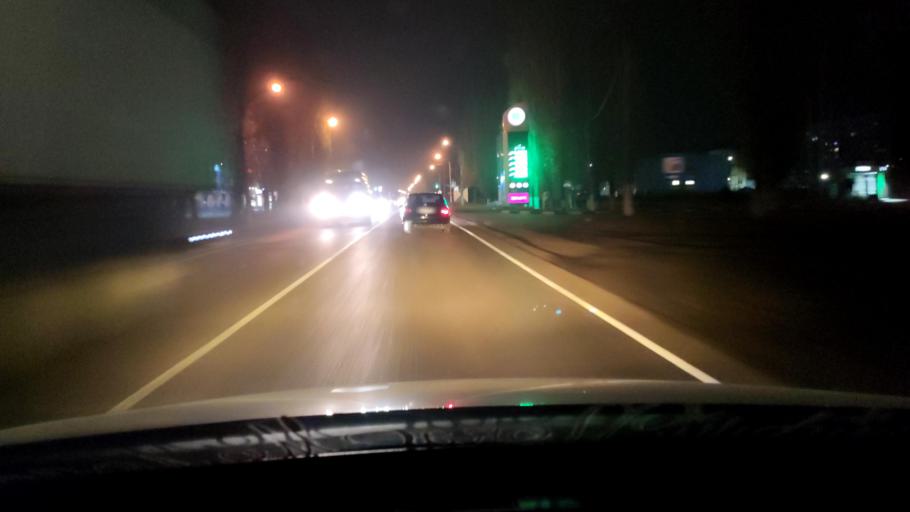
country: RU
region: Voronezj
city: Semiluki
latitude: 51.6996
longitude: 39.0158
